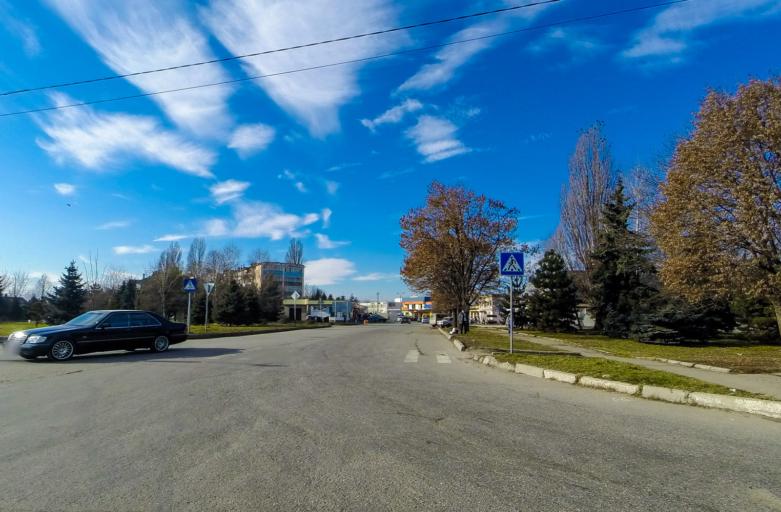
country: RU
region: Kabardino-Balkariya
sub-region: Gorod Nal'chik
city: Nal'chik
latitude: 43.5203
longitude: 43.6126
